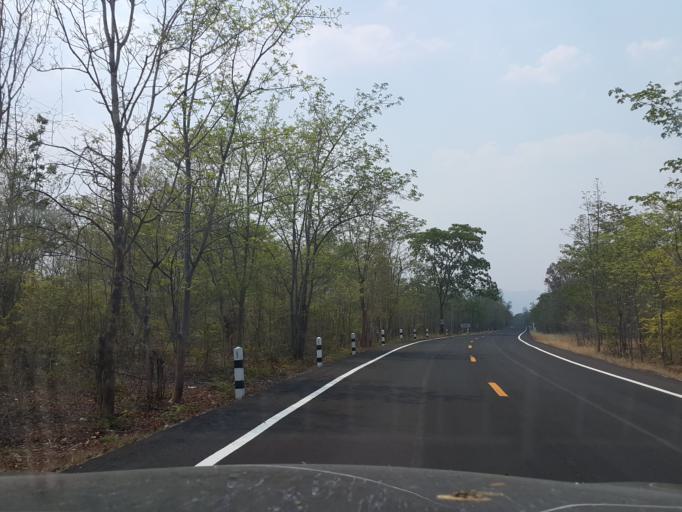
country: TH
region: Lampang
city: Mae Phrik
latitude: 17.4806
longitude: 99.1097
